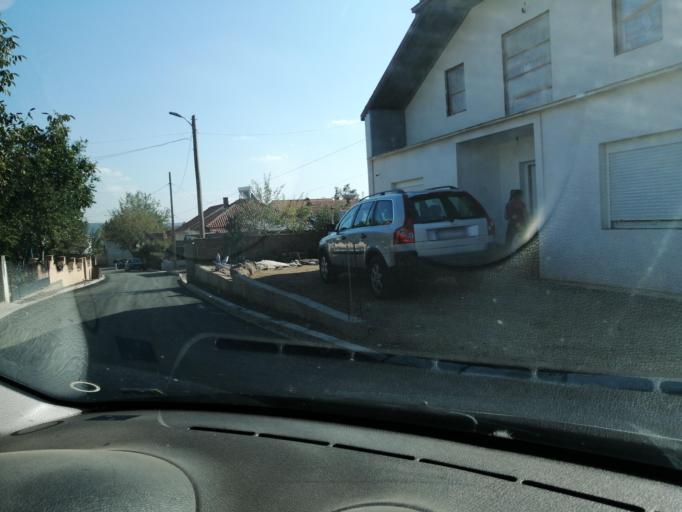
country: MK
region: Bogdanci
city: Bogdanci
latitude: 41.2055
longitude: 22.5668
